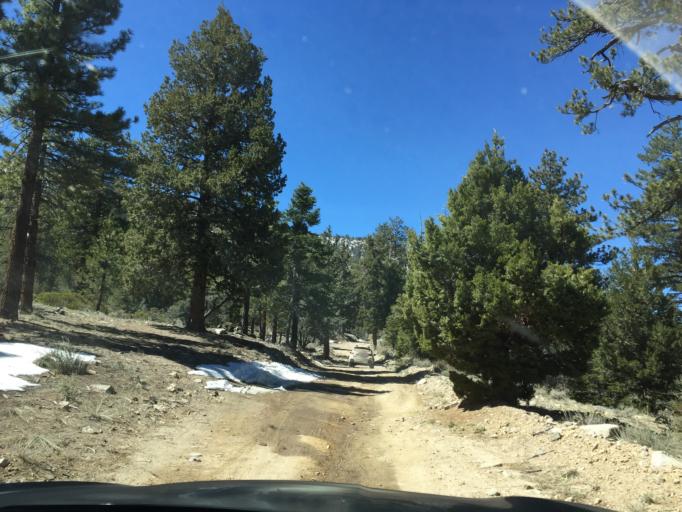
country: US
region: California
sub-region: San Bernardino County
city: Big Bear City
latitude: 34.2074
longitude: -116.7322
